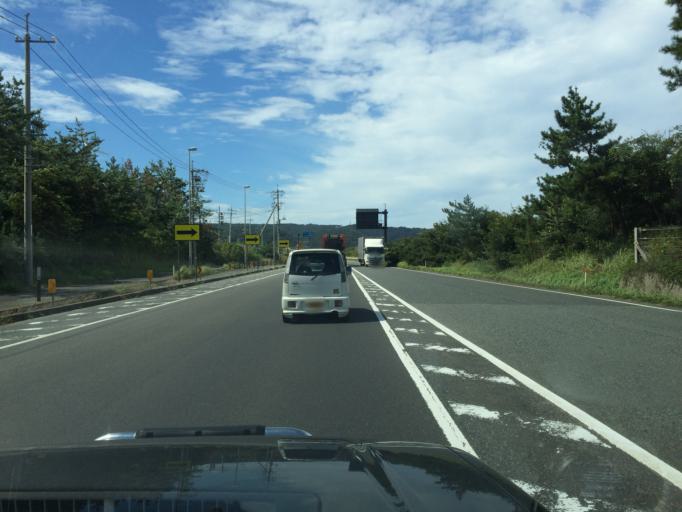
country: JP
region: Tottori
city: Tottori
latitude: 35.5178
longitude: 134.0438
